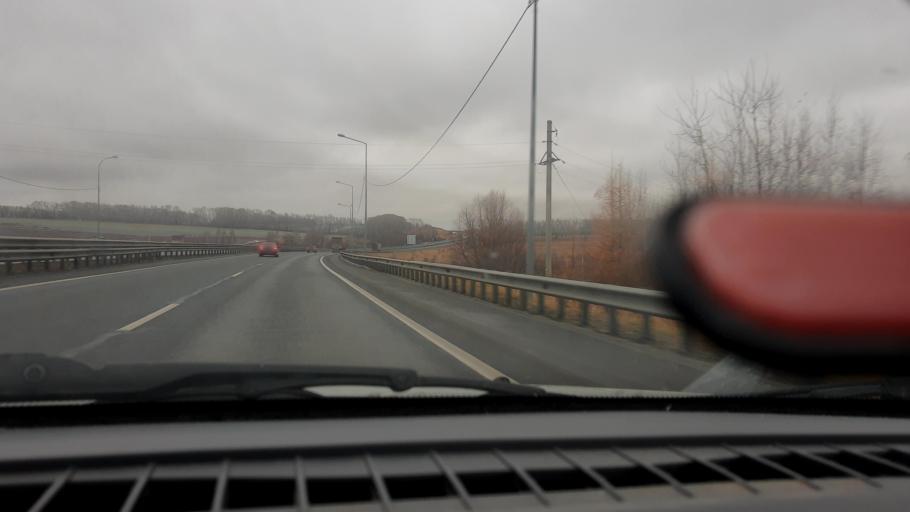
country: RU
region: Nizjnij Novgorod
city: Burevestnik
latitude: 56.1669
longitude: 43.7493
